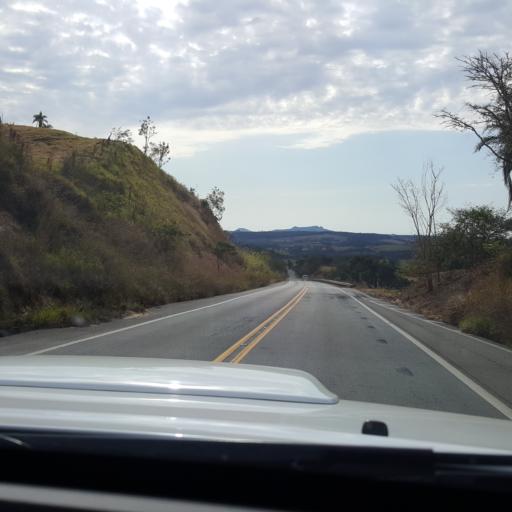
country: BR
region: Sao Paulo
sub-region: Itaporanga
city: Itaporanga
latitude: -23.7374
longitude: -49.4564
